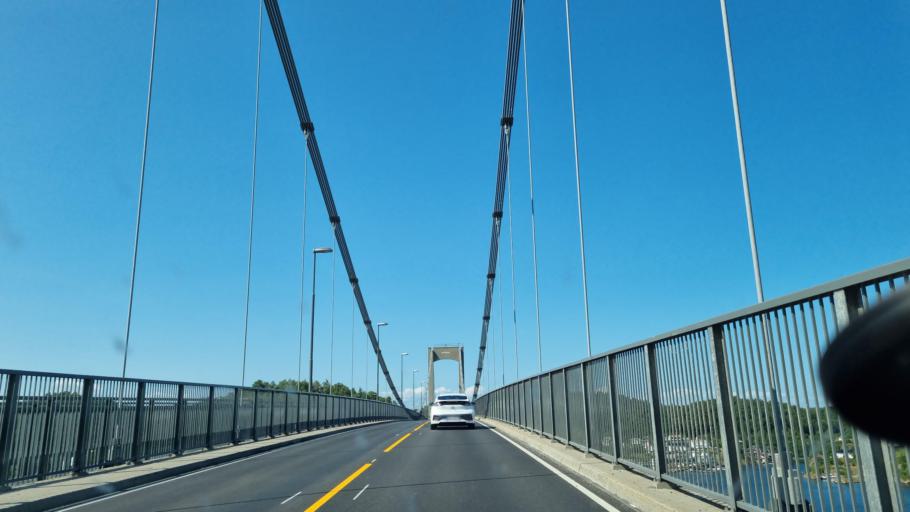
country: NO
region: Aust-Agder
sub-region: Arendal
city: Arendal
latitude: 58.4700
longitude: 8.8234
